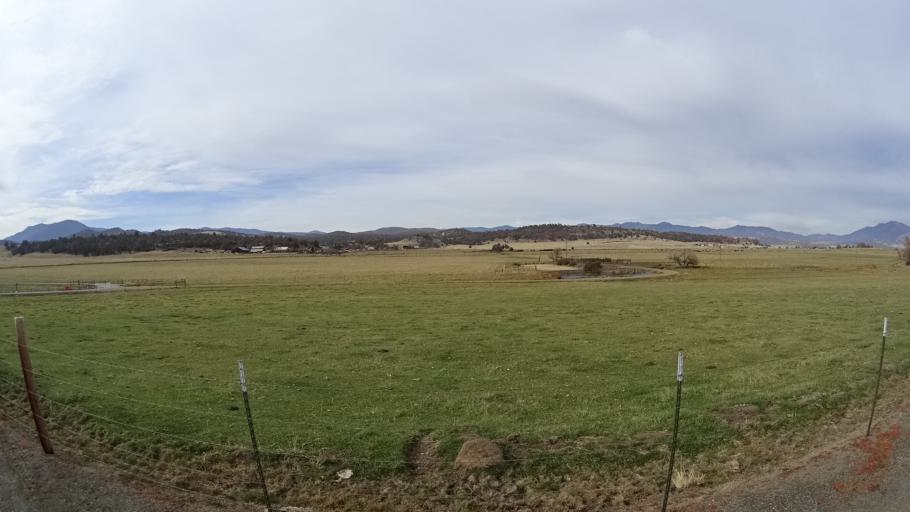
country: US
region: California
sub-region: Siskiyou County
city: Montague
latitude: 41.6952
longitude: -122.5543
